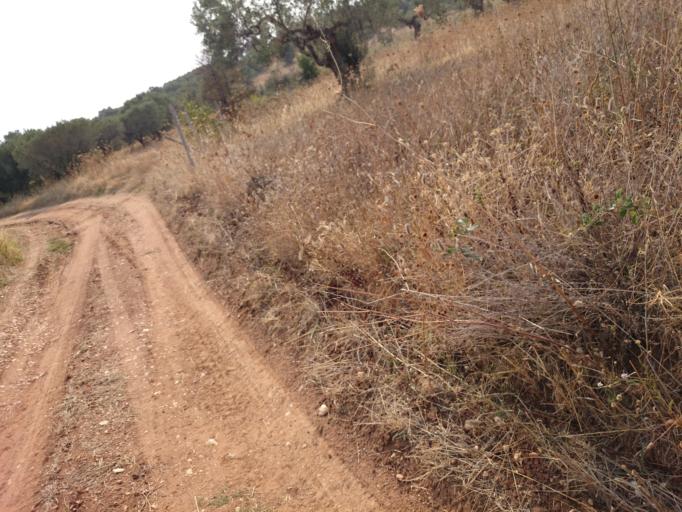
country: GR
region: Central Macedonia
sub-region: Nomos Chalkidikis
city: Nea Moudhania
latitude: 40.2555
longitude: 23.2715
